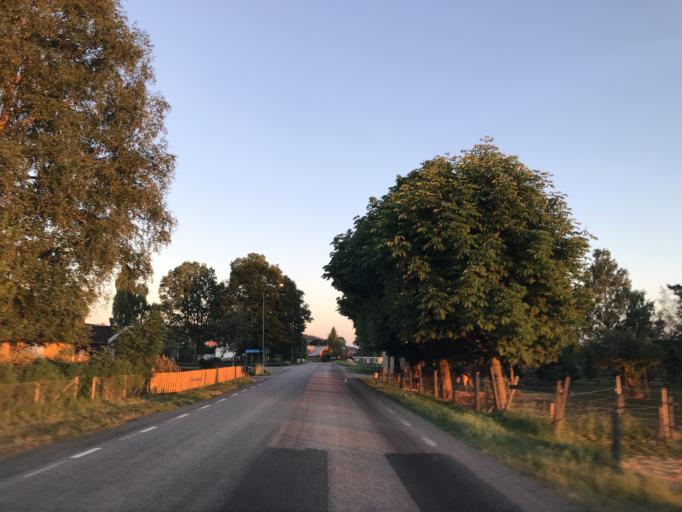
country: SE
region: Vaestra Goetaland
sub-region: Marks Kommun
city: Horred
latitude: 57.4281
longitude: 12.5201
